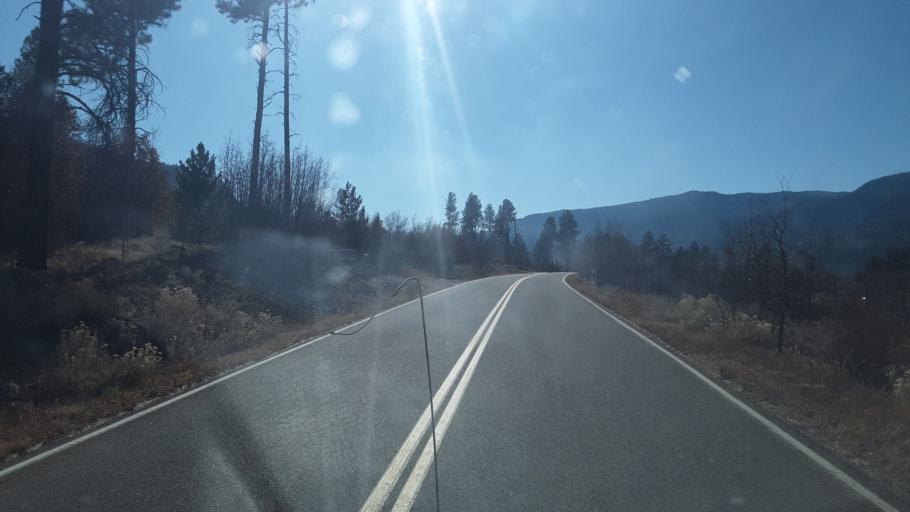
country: US
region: Colorado
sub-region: La Plata County
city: Durango
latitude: 37.4130
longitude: -107.8097
